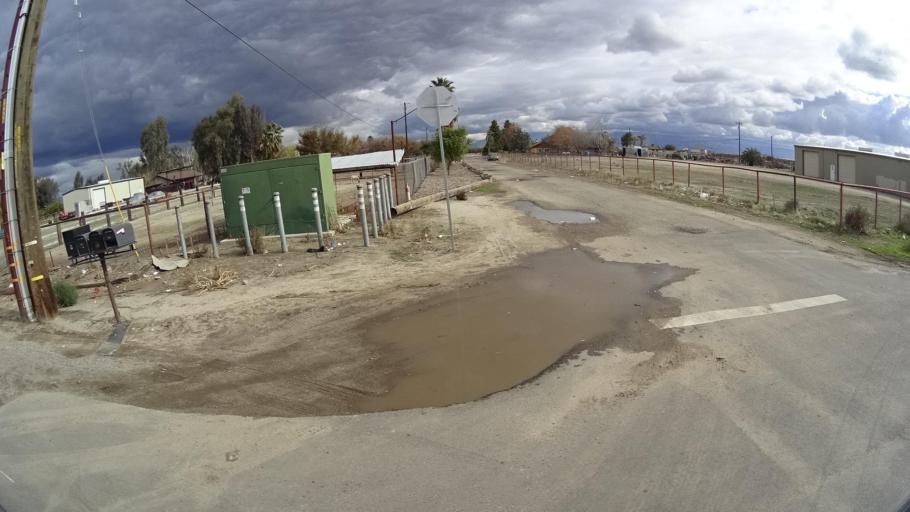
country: US
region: California
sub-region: Kern County
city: Greenfield
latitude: 35.2740
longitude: -119.0030
